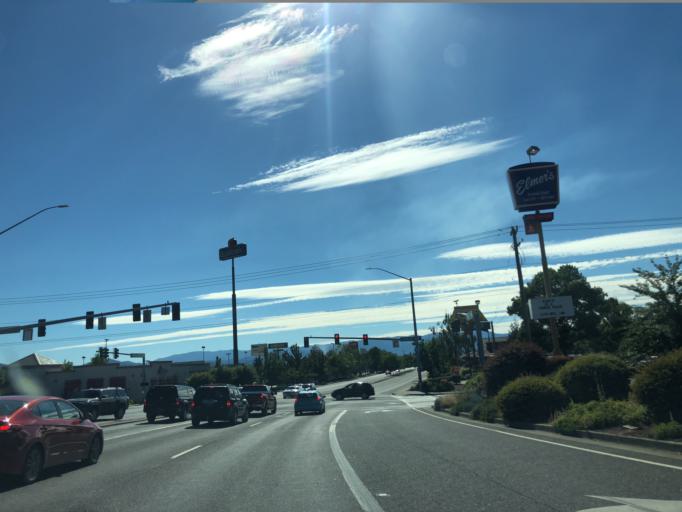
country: US
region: Oregon
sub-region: Josephine County
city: Fruitdale
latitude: 42.4366
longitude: -123.2972
